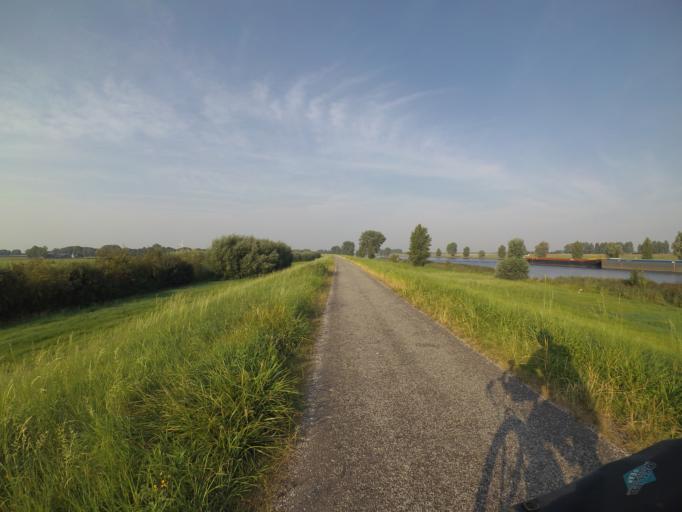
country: NL
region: North Brabant
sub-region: Gemeente Heusden
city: Heusden
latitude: 51.7278
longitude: 5.0961
